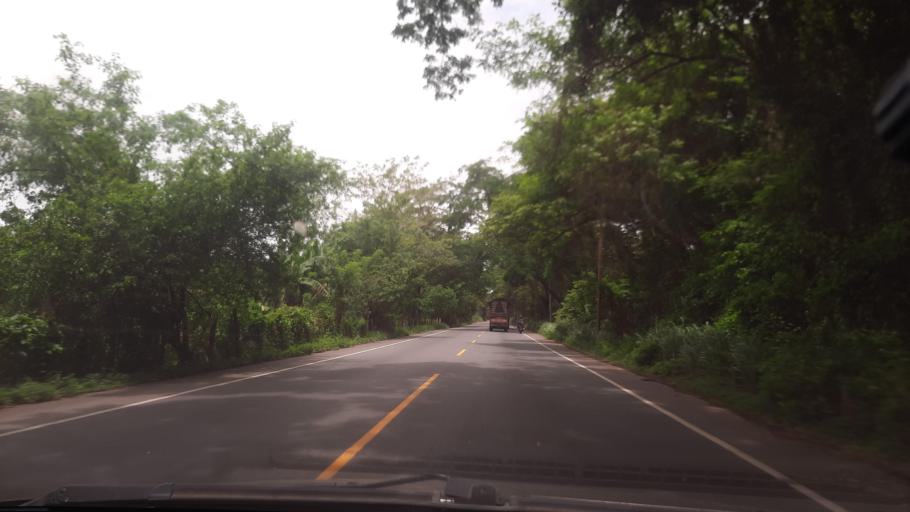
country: GT
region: Izabal
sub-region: Municipio de Los Amates
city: Los Amates
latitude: 15.2108
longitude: -89.2390
